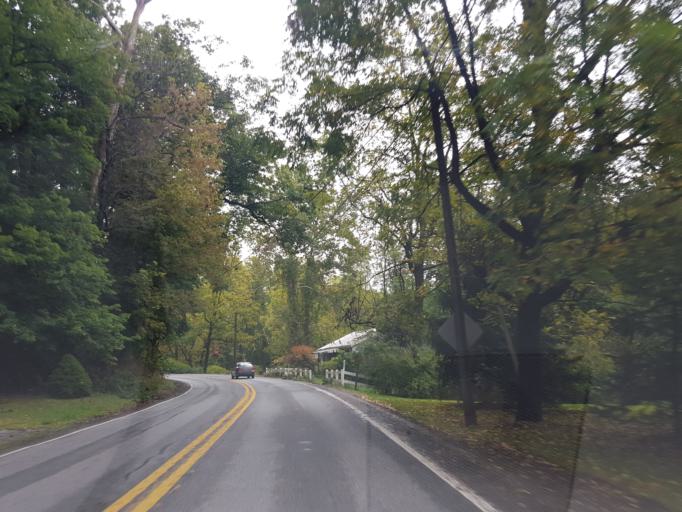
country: US
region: Pennsylvania
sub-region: York County
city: Valley View
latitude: 39.9476
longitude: -76.6767
